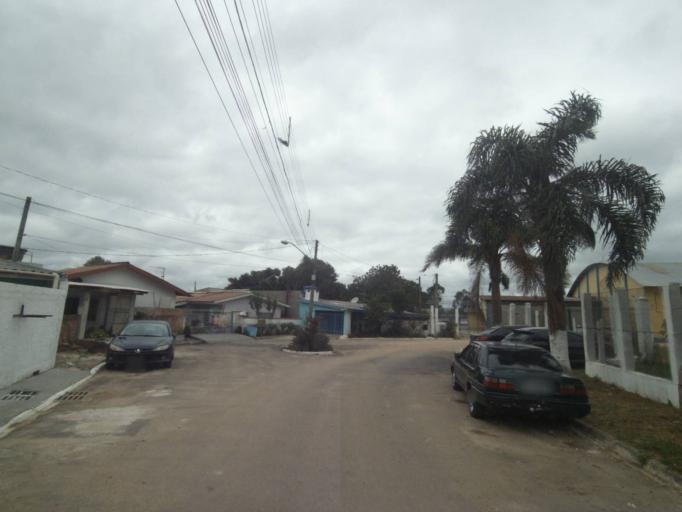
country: BR
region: Parana
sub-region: Sao Jose Dos Pinhais
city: Sao Jose dos Pinhais
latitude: -25.5529
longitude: -49.2723
